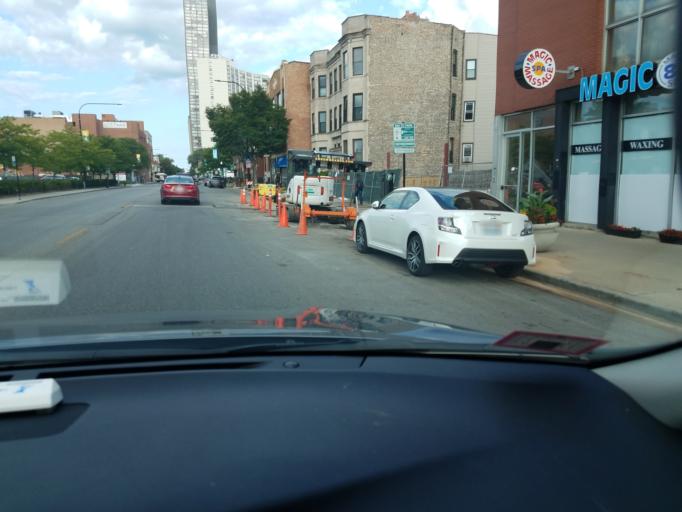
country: US
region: Illinois
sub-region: Cook County
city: Lincolnwood
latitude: 41.9545
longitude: -87.6537
